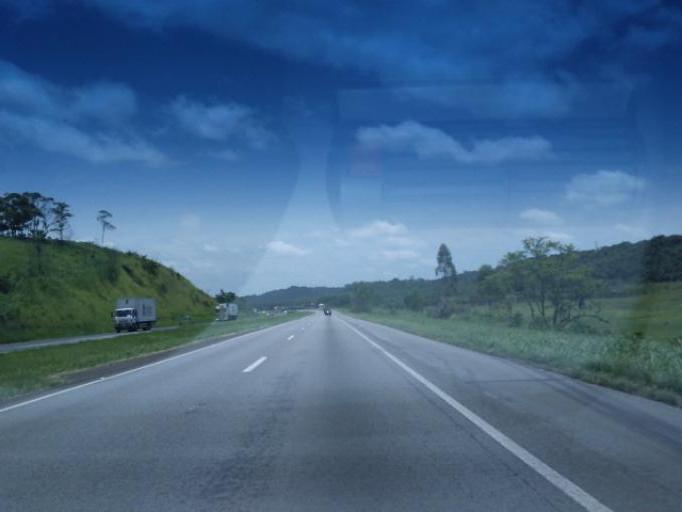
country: BR
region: Sao Paulo
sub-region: Registro
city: Registro
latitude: -24.4211
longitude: -47.7735
